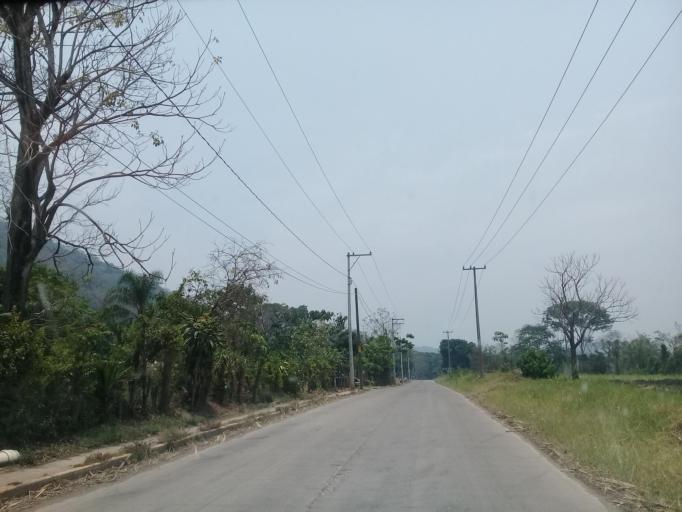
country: MX
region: Veracruz
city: Cosolapa
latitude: 18.5900
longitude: -96.6964
